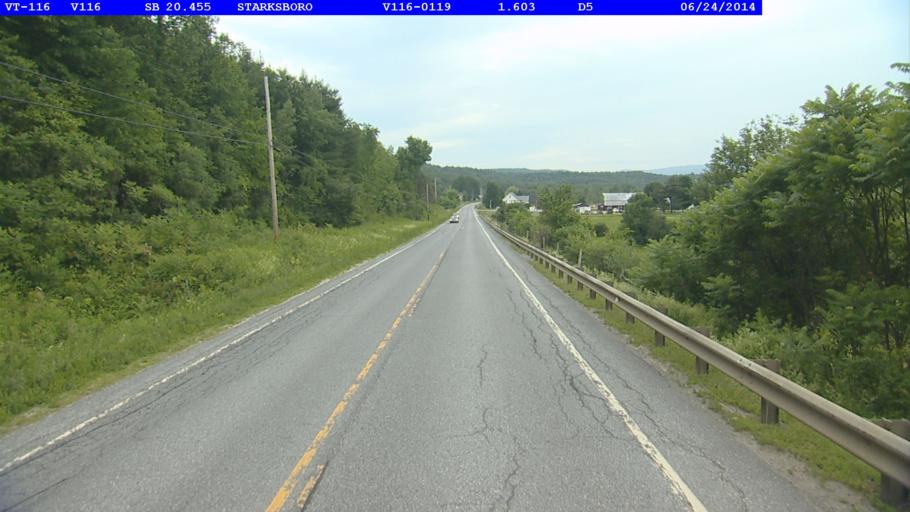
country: US
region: Vermont
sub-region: Addison County
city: Bristol
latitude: 44.2078
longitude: -73.0532
